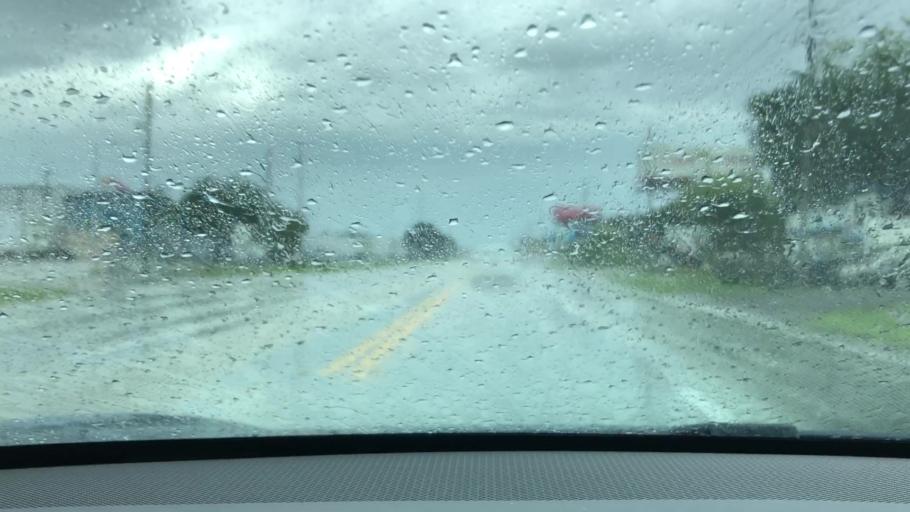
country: US
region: Florida
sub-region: Orange County
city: Belle Isle
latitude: 28.4583
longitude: -81.3657
